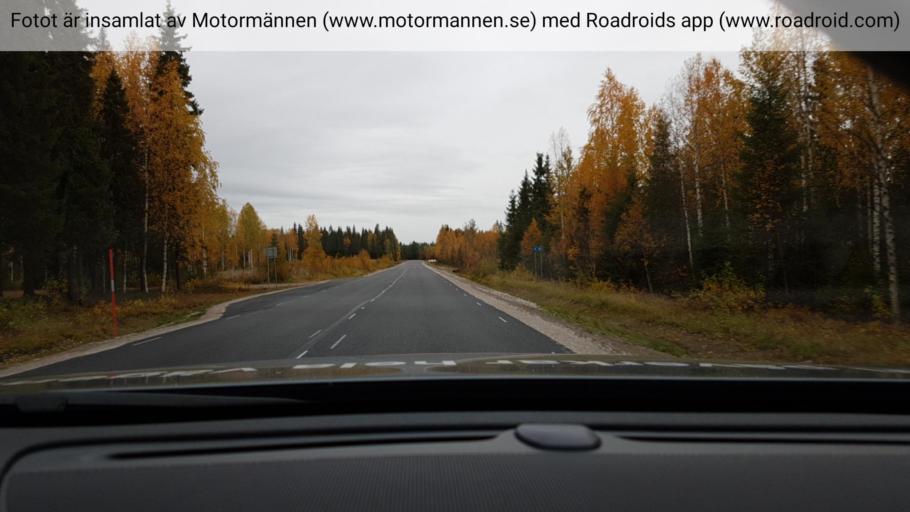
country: SE
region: Norrbotten
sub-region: Overkalix Kommun
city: OEverkalix
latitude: 66.4130
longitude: 22.8049
